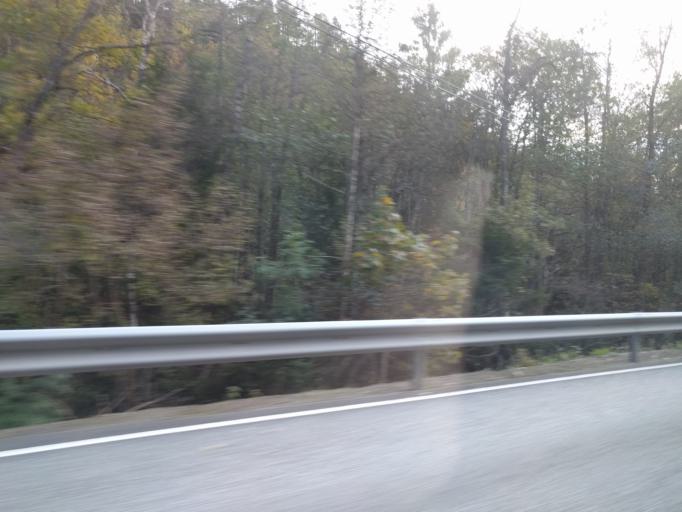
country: NO
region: Vest-Agder
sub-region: Kristiansand
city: Strai
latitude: 58.2437
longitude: 7.8782
